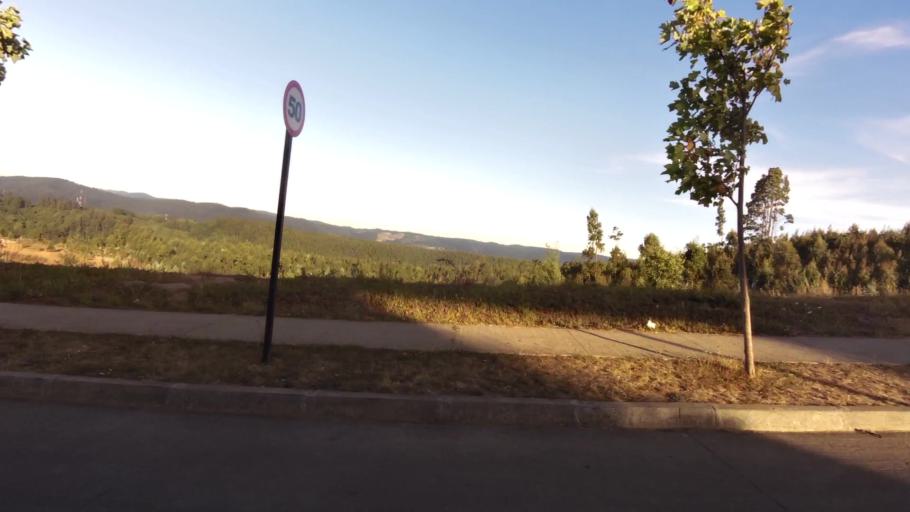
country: CL
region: Biobio
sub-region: Provincia de Concepcion
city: Concepcion
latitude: -36.8601
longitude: -73.0902
